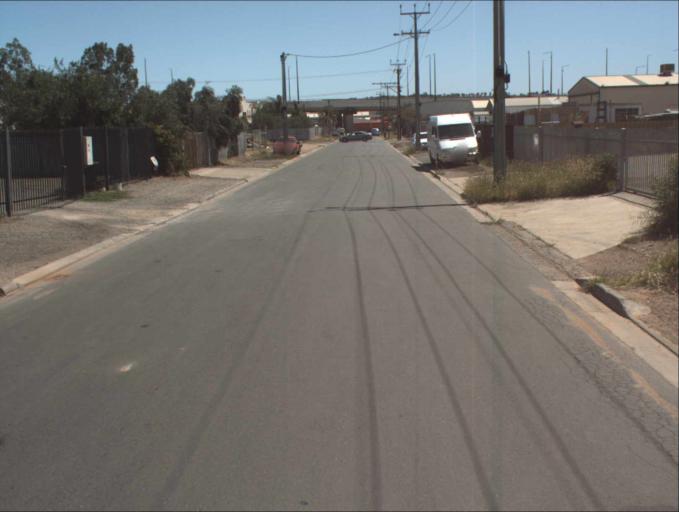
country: AU
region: South Australia
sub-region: Port Adelaide Enfield
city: Blair Athol
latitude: -34.8349
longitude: 138.5656
